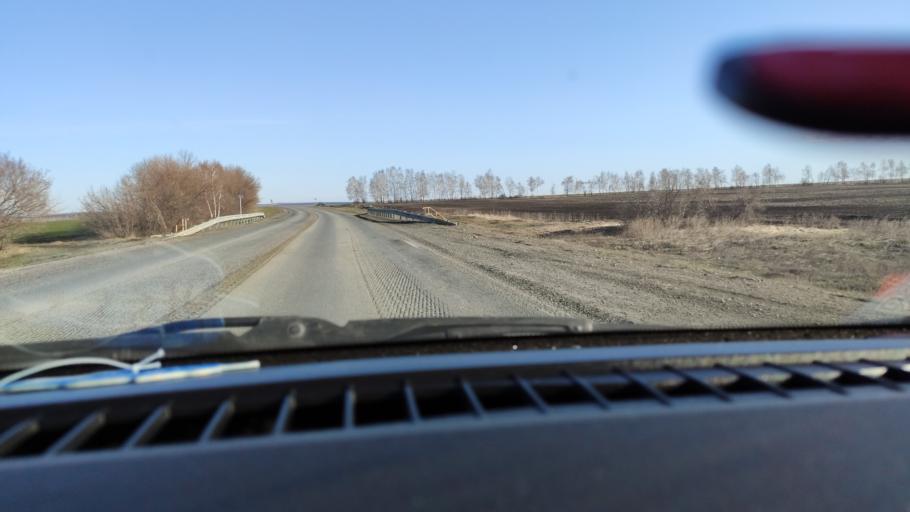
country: RU
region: Saratov
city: Dukhovnitskoye
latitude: 52.7174
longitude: 48.2660
